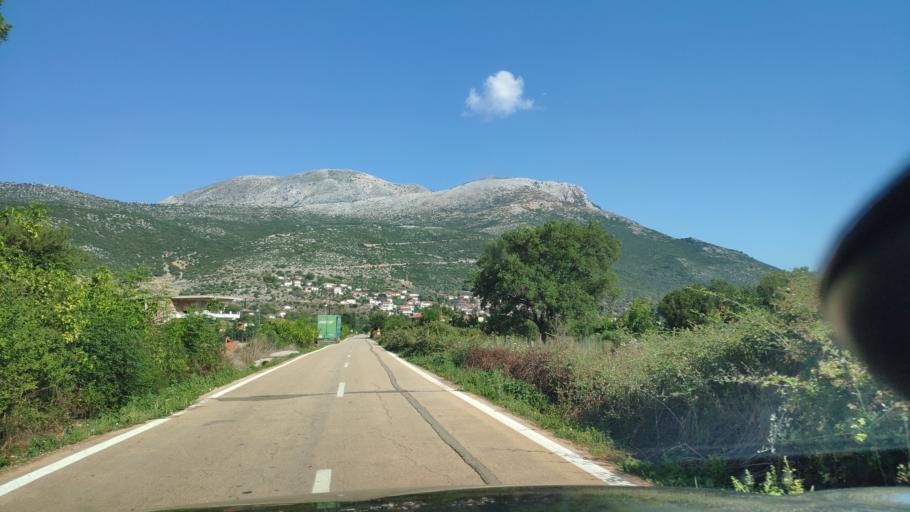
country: GR
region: West Greece
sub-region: Nomos Aitolias kai Akarnanias
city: Archontochorion
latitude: 38.7017
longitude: 21.0915
